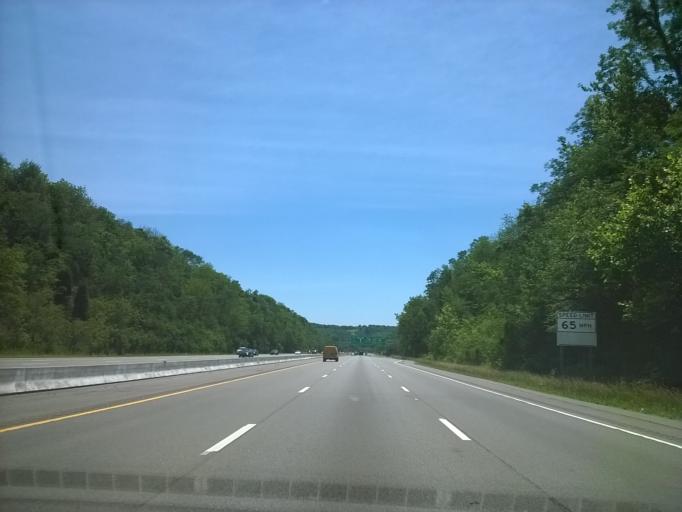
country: US
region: Ohio
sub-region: Hamilton County
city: Miamitown
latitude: 39.2102
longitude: -84.7186
